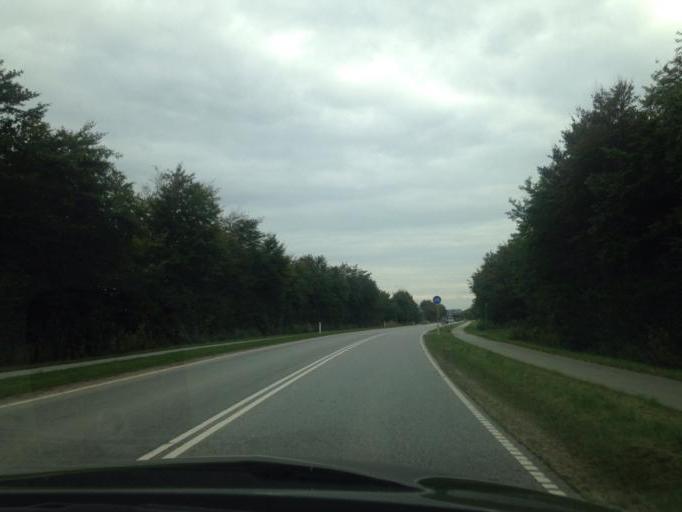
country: DK
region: South Denmark
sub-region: Haderslev Kommune
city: Haderslev
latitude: 55.2467
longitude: 9.4290
